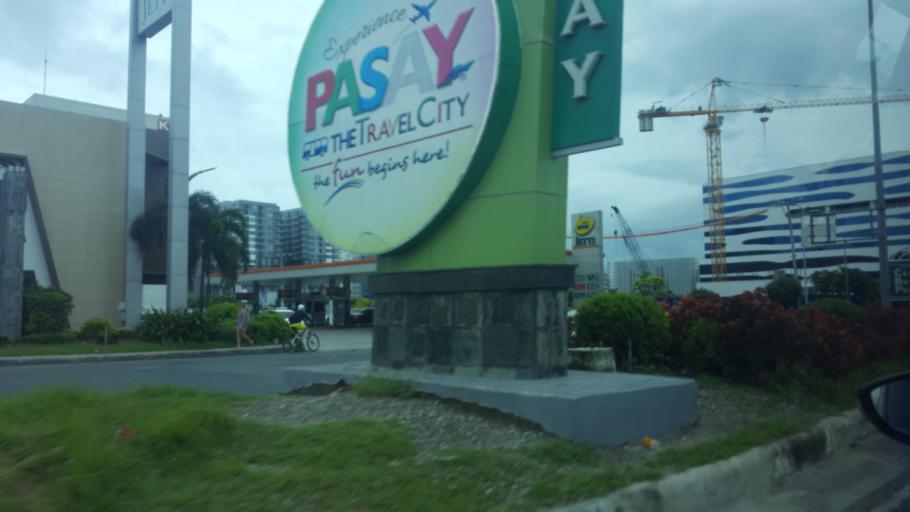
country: PH
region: Metro Manila
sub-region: Makati City
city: Makati City
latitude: 14.5312
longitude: 120.9897
